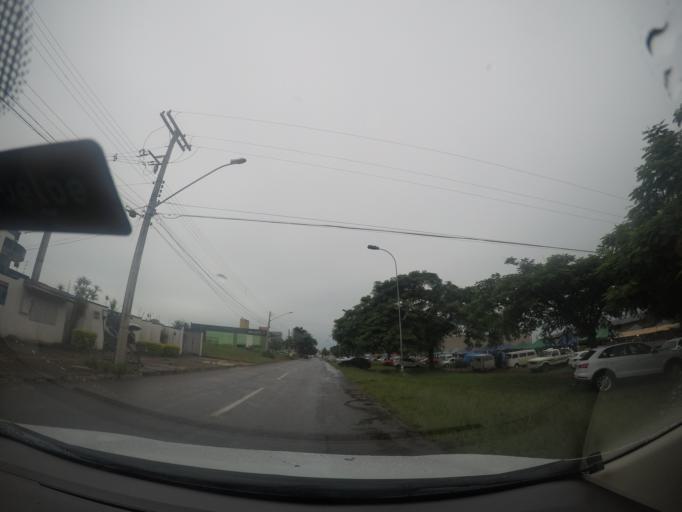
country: BR
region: Goias
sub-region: Goiania
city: Goiania
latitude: -16.6416
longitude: -49.2380
